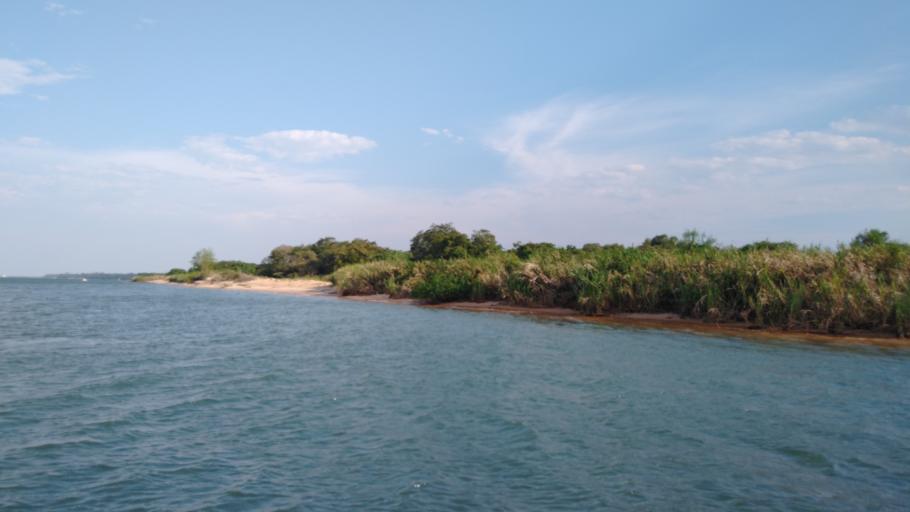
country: PY
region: Neembucu
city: Cerrito
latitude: -27.3476
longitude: -57.6830
